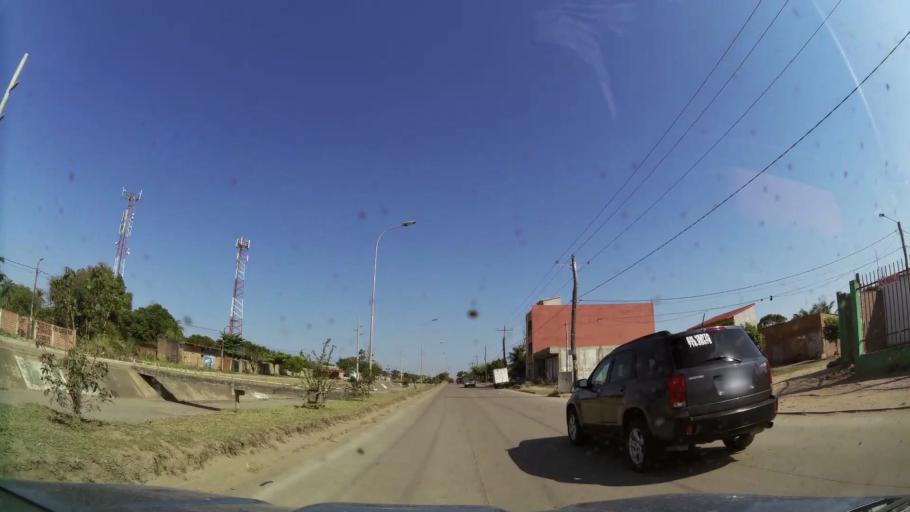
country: BO
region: Santa Cruz
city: Cotoca
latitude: -17.7935
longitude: -63.1087
